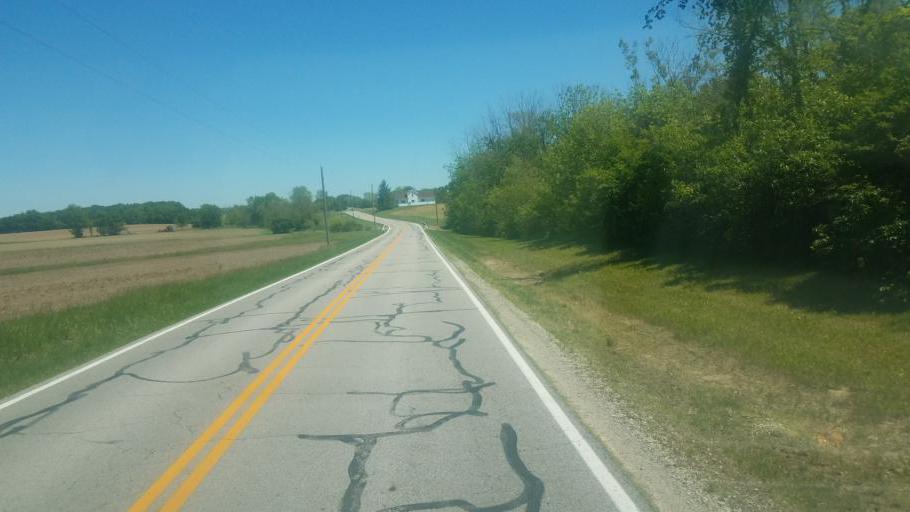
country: US
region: Ohio
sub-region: Miami County
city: Piqua
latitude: 40.2107
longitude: -84.2869
